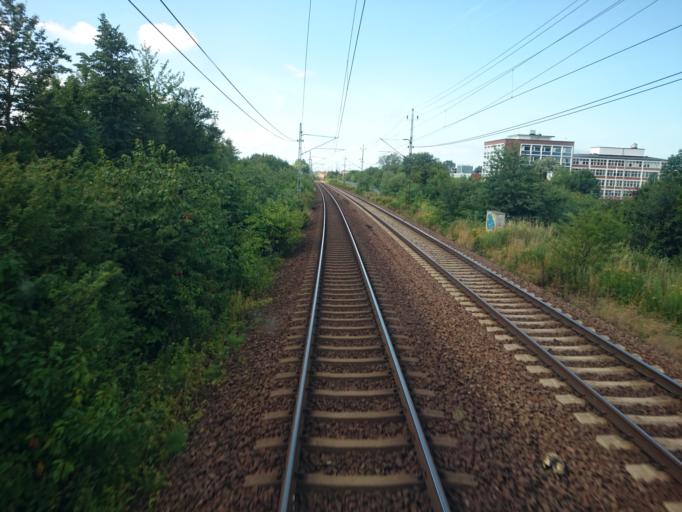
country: SE
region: Skane
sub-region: Lunds Kommun
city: Lund
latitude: 55.6970
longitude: 13.1758
